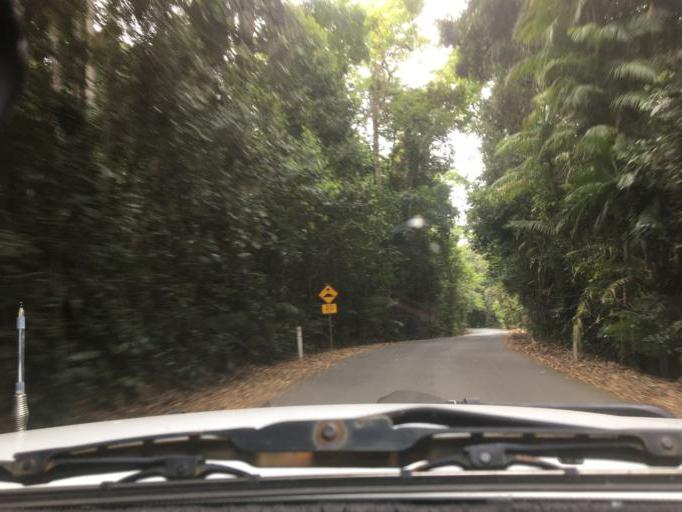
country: AU
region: Queensland
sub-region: Tablelands
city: Tolga
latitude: -17.2818
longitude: 145.6284
